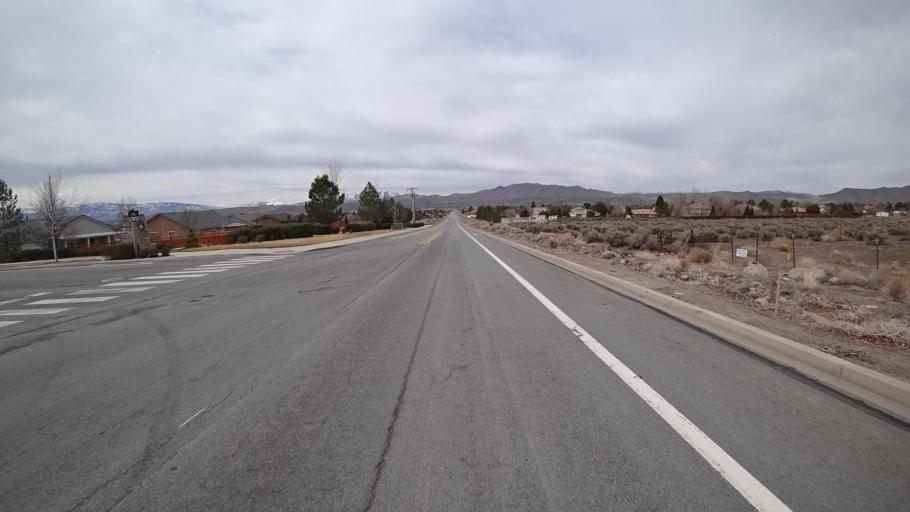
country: US
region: Nevada
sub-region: Washoe County
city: Spanish Springs
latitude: 39.6363
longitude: -119.6762
